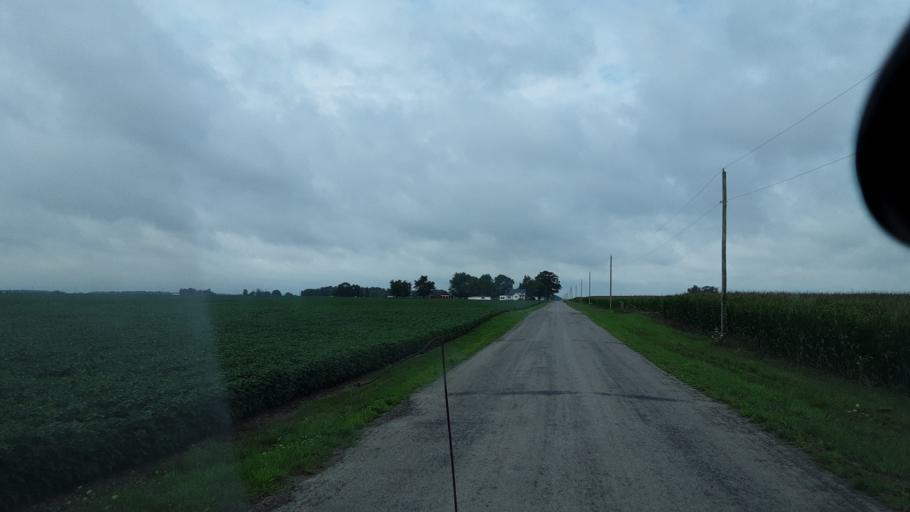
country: US
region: Indiana
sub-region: Allen County
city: Monroeville
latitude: 40.9213
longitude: -84.8509
